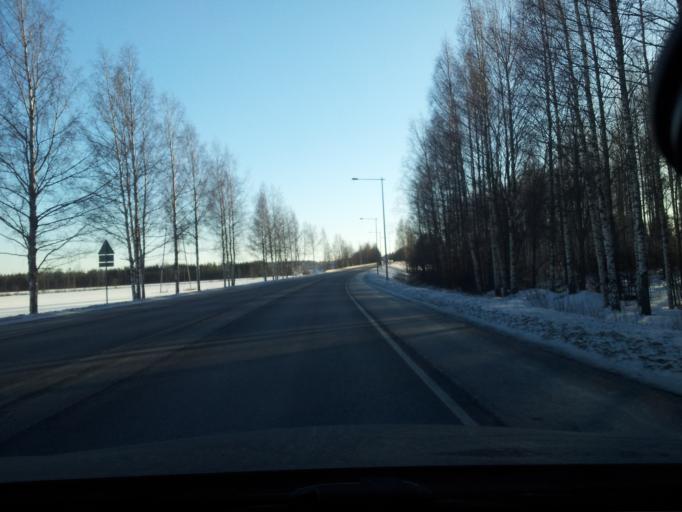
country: FI
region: Uusimaa
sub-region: Helsinki
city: Vihti
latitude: 60.3441
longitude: 24.3328
